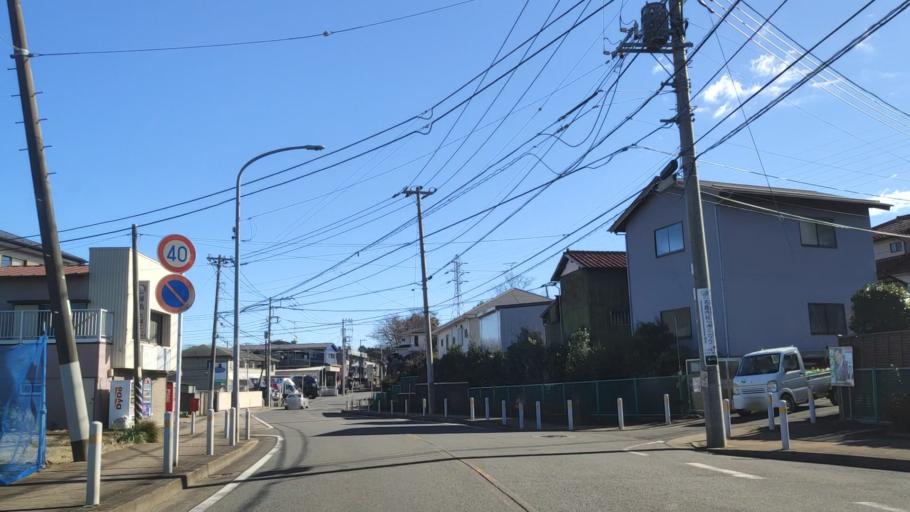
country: JP
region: Kanagawa
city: Yokohama
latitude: 35.4998
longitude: 139.5950
